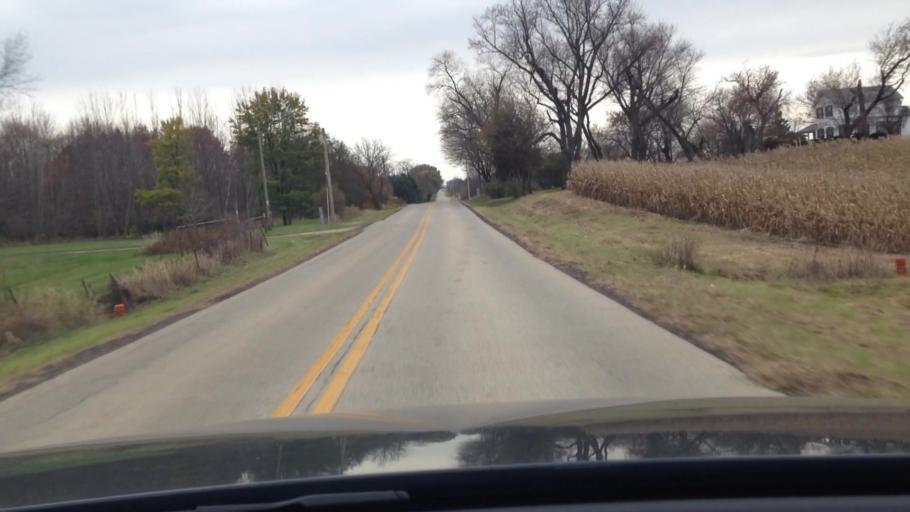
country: US
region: Illinois
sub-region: McHenry County
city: Woodstock
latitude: 42.2898
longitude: -88.4770
